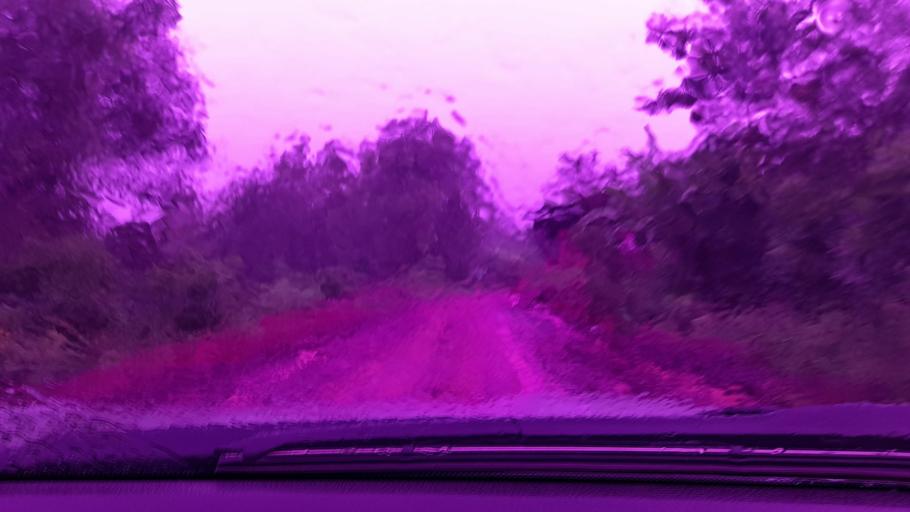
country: ET
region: Oromiya
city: Metu
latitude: 8.3498
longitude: 35.5986
